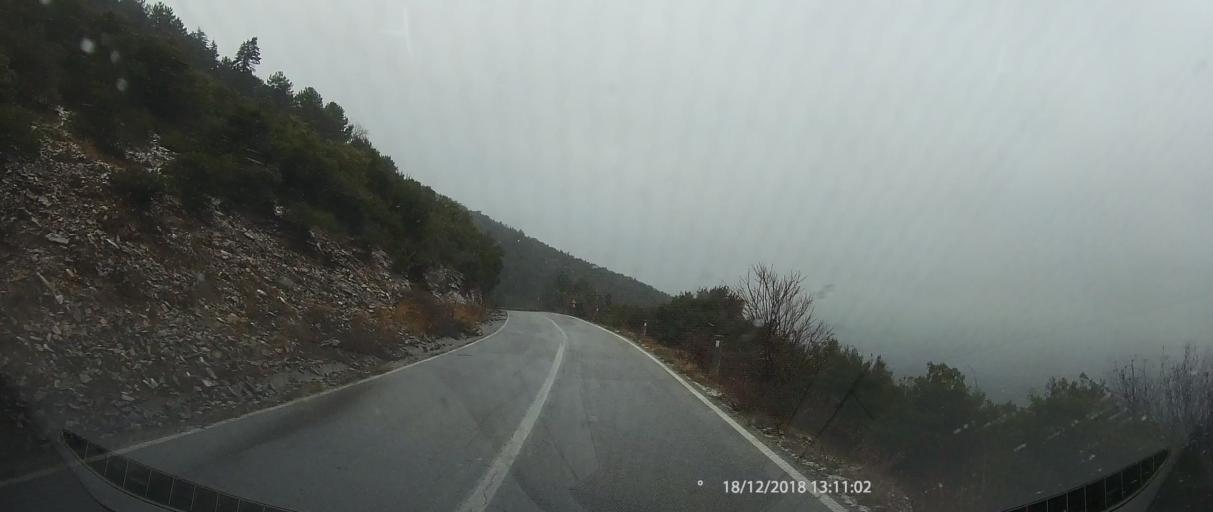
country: GR
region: Central Macedonia
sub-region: Nomos Pierias
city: Litochoro
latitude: 40.1095
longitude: 22.4800
